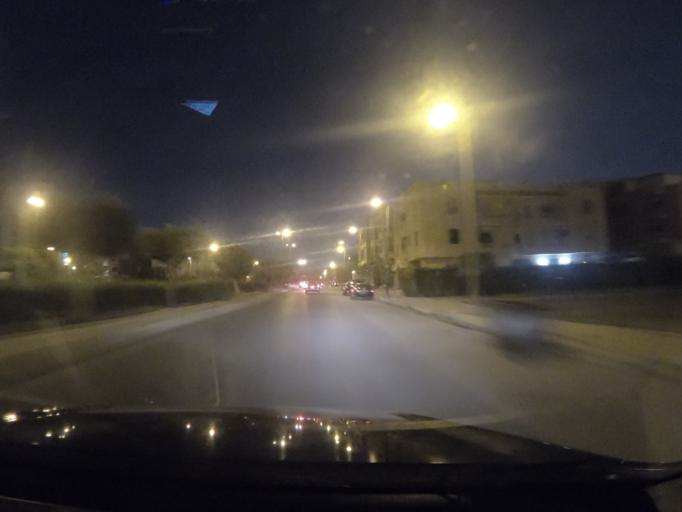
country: EG
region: Muhafazat al Qahirah
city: Cairo
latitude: 30.0139
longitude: 31.4234
